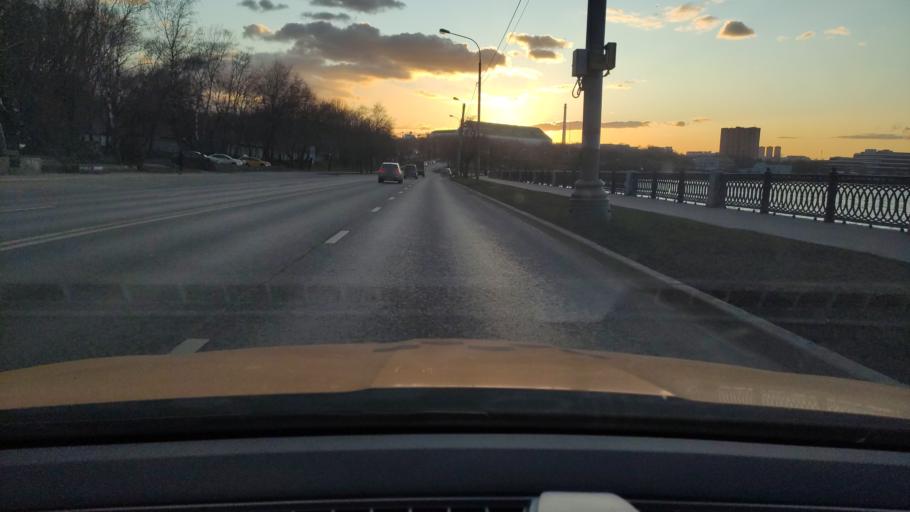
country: RU
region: Moskovskaya
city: Kozhukhovo
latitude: 55.6841
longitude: 37.6419
